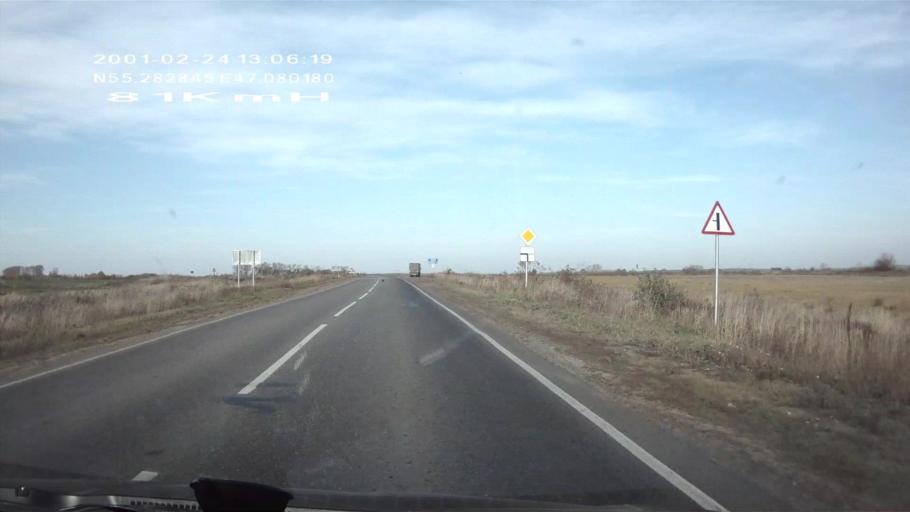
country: RU
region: Chuvashia
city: Ibresi
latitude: 55.2829
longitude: 47.0801
